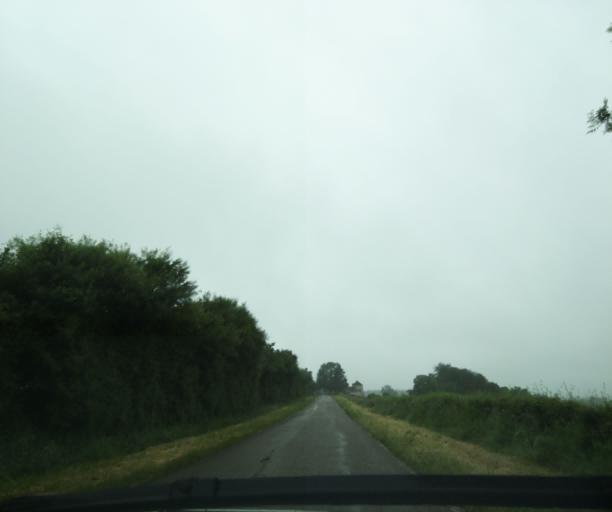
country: FR
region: Bourgogne
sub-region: Departement de Saone-et-Loire
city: Charolles
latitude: 46.4243
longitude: 4.2776
